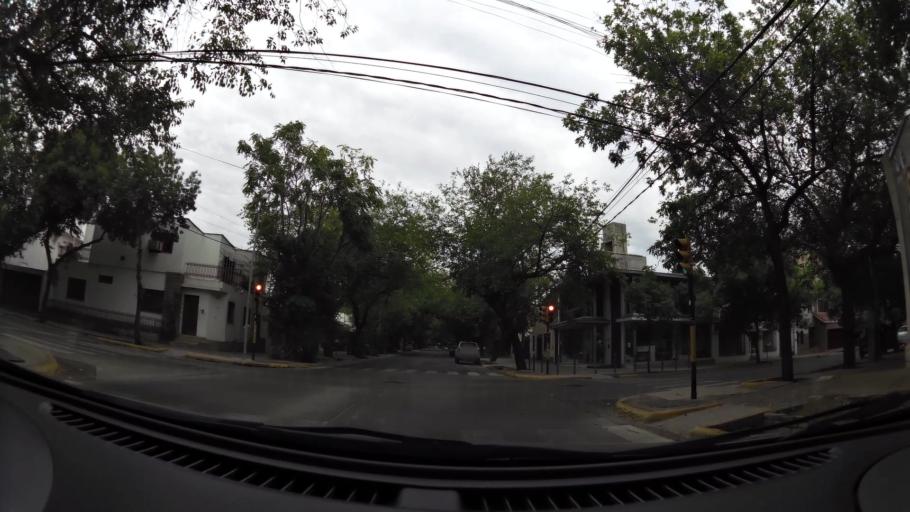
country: AR
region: Mendoza
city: Mendoza
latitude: -32.9027
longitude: -68.8635
